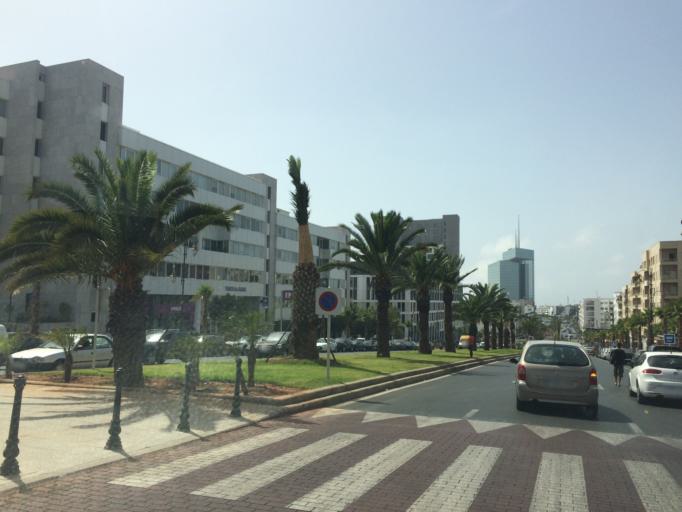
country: MA
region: Rabat-Sale-Zemmour-Zaer
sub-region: Skhirate-Temara
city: Temara
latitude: 33.9537
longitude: -6.8642
